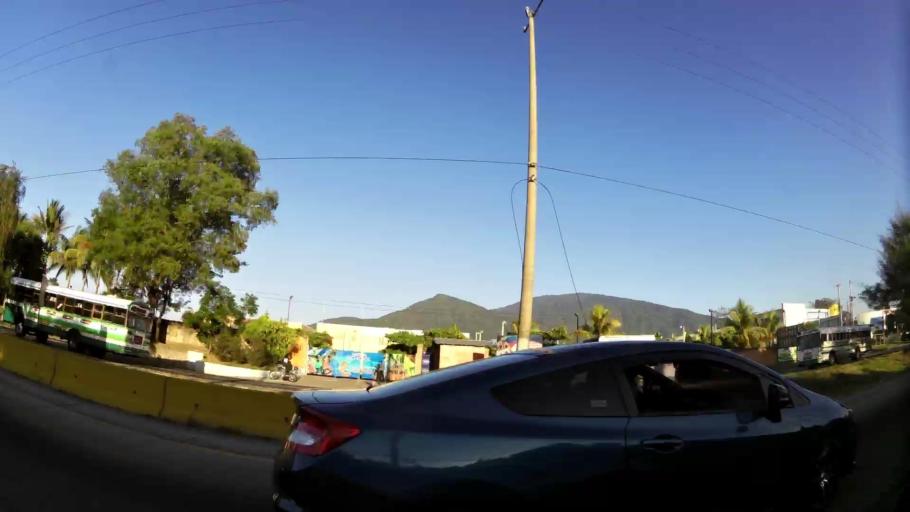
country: SV
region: La Libertad
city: Santa Tecla
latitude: 13.7439
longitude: -89.3634
